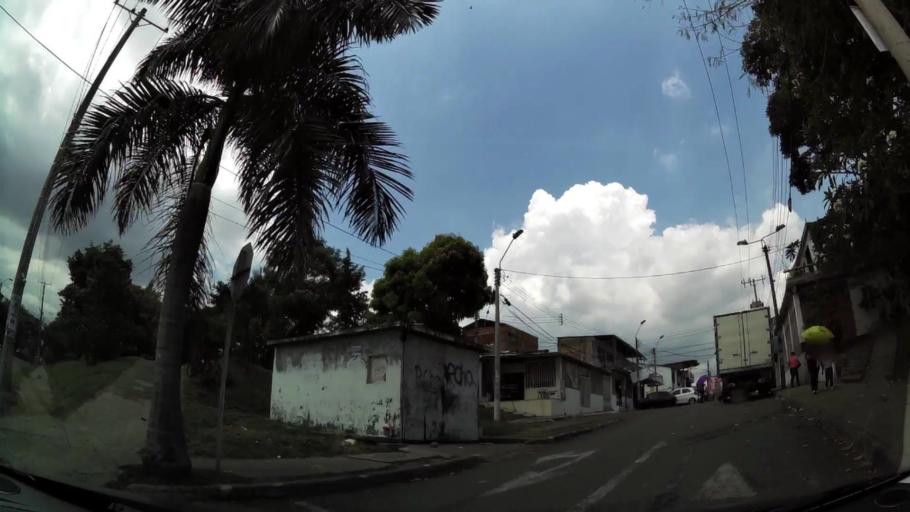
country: CO
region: Valle del Cauca
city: Cali
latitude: 3.4679
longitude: -76.4839
